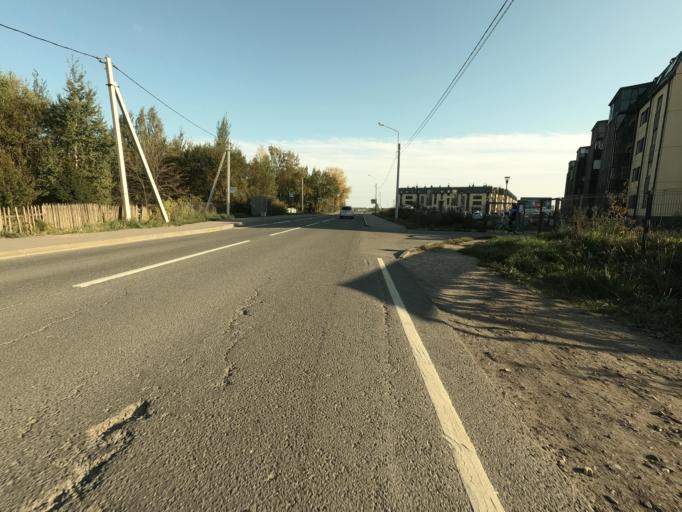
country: RU
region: St.-Petersburg
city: Pontonnyy
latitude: 59.7569
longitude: 30.6294
